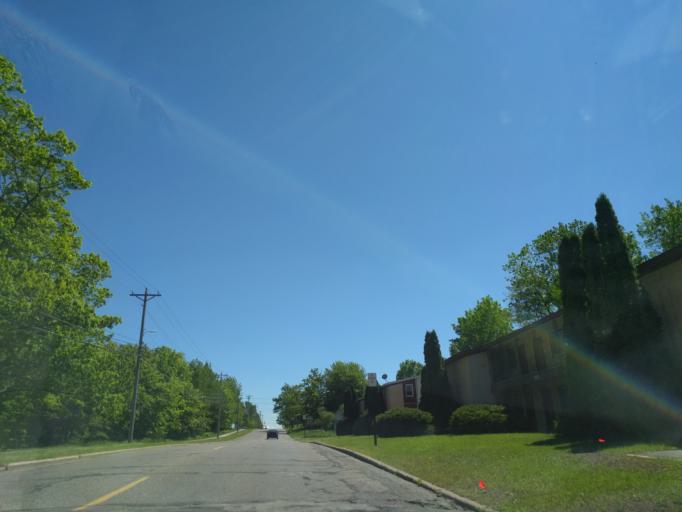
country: US
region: Michigan
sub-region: Marquette County
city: Marquette
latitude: 46.5518
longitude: -87.4123
